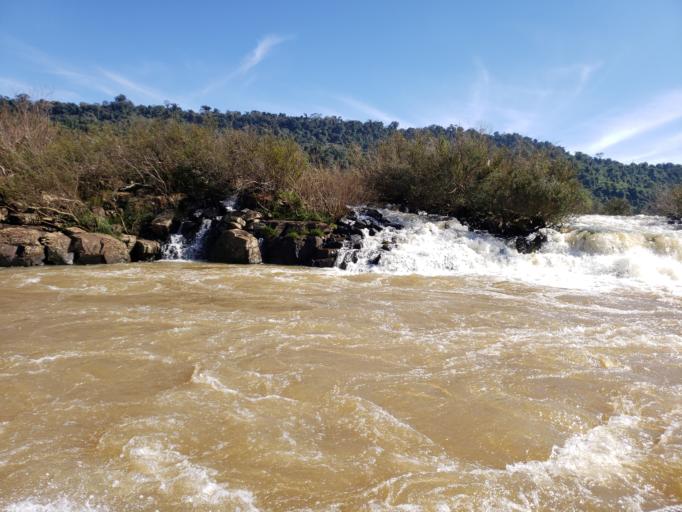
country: BR
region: Rio Grande do Sul
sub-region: Tres Passos
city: Tres Passos
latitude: -27.1476
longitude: -53.8868
